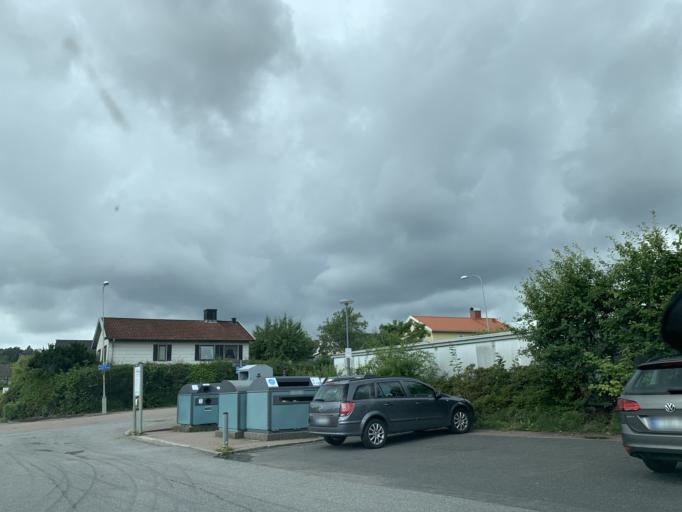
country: SE
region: Vaestra Goetaland
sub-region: Goteborg
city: Eriksbo
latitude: 57.7457
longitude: 12.0497
